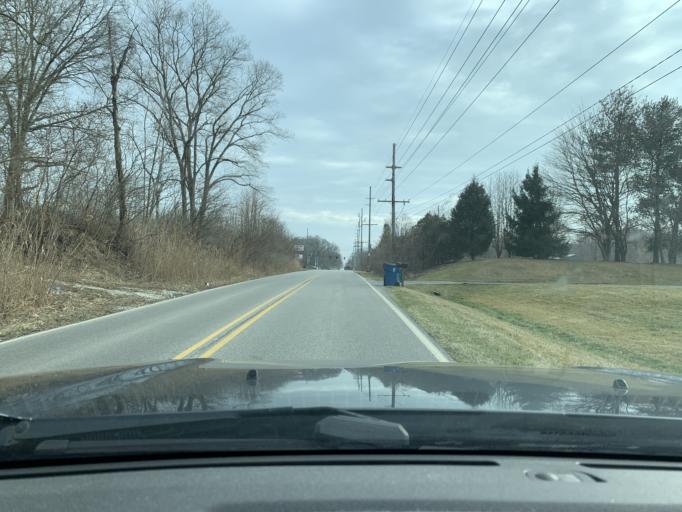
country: US
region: Indiana
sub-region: Porter County
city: Chesterton
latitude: 41.5522
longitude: -87.0664
